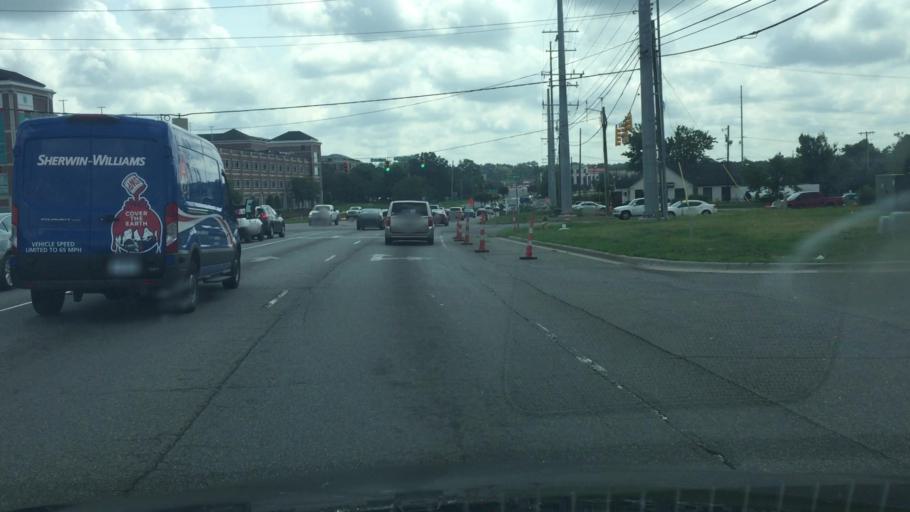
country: US
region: North Carolina
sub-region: Cabarrus County
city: Concord
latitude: 35.4383
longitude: -80.6055
